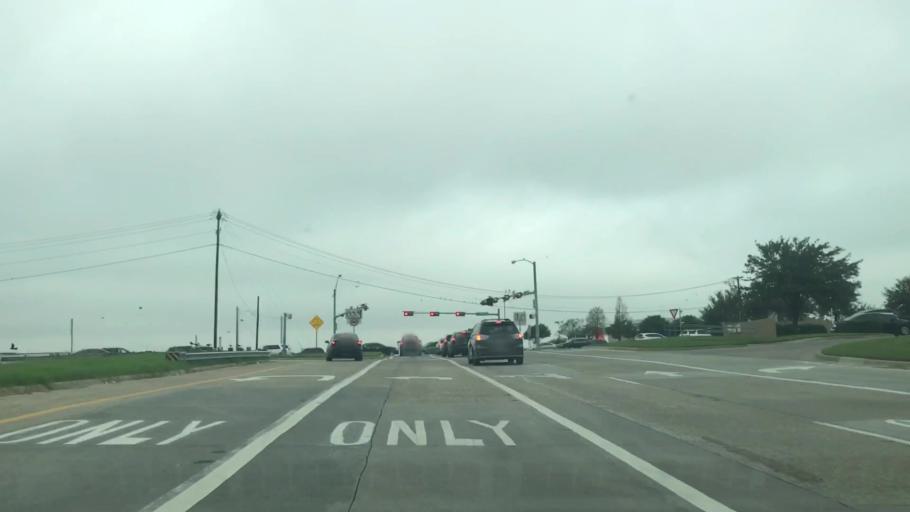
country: US
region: Texas
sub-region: Dallas County
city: Farmers Branch
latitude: 32.9161
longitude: -96.9576
